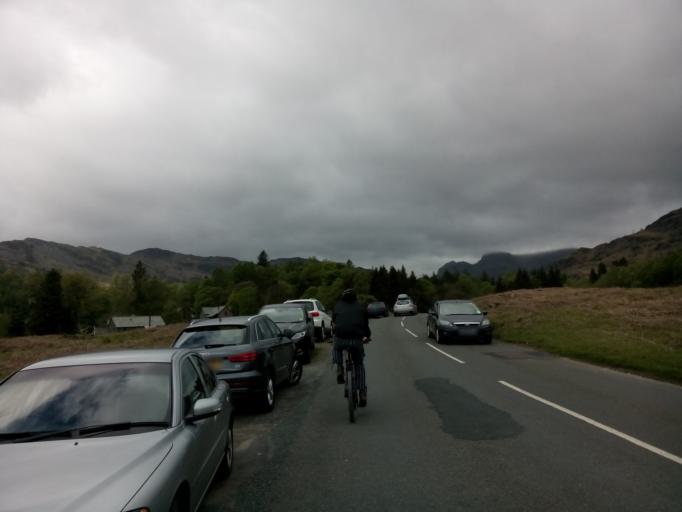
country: GB
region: England
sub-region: Cumbria
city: Ambleside
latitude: 54.4354
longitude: -3.0333
